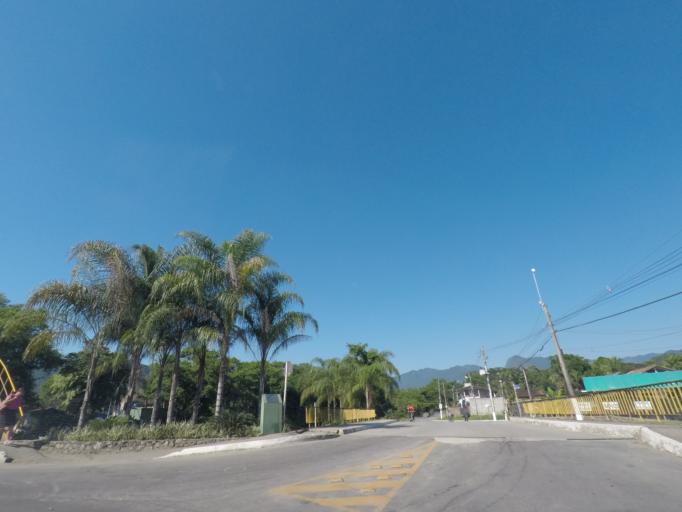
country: BR
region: Rio de Janeiro
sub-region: Parati
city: Paraty
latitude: -23.2182
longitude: -44.7234
